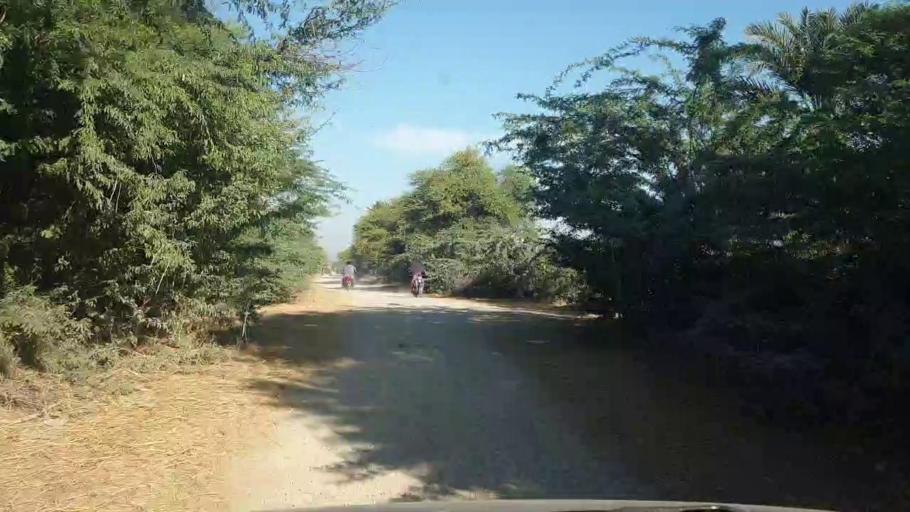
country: PK
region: Sindh
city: Talhar
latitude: 24.9043
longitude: 68.8112
